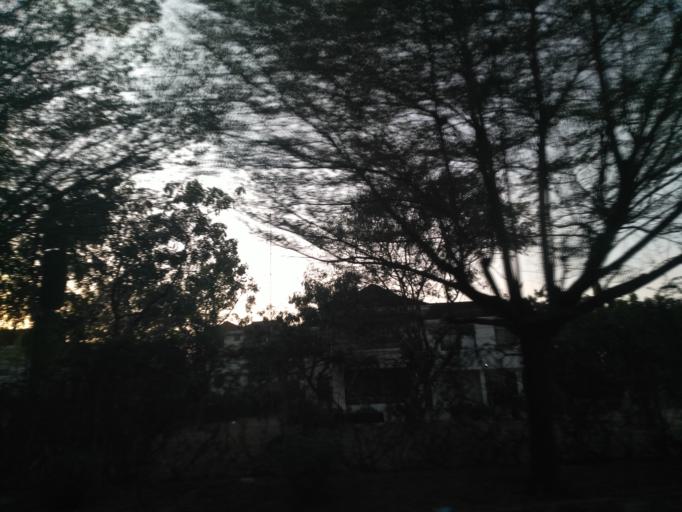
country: TZ
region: Dar es Salaam
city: Magomeni
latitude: -6.7747
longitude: 39.2520
